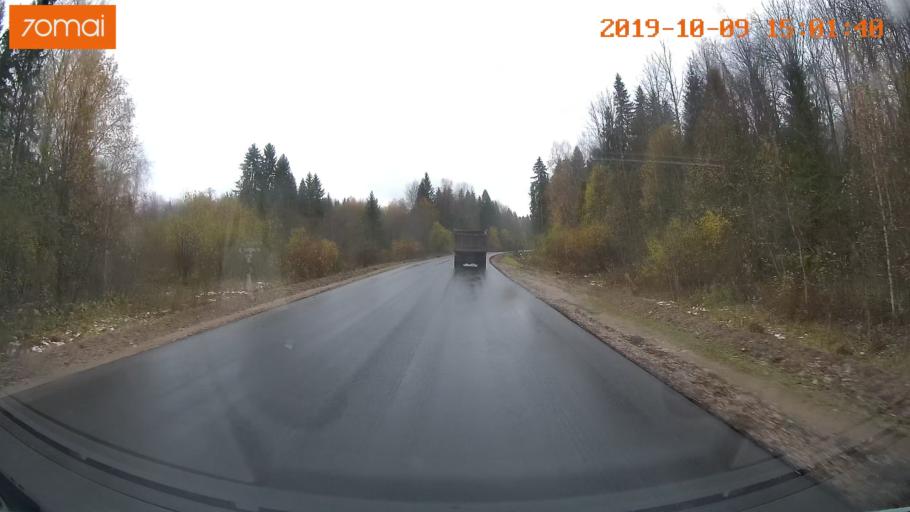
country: RU
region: Kostroma
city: Chistyye Bory
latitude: 58.2943
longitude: 41.6811
